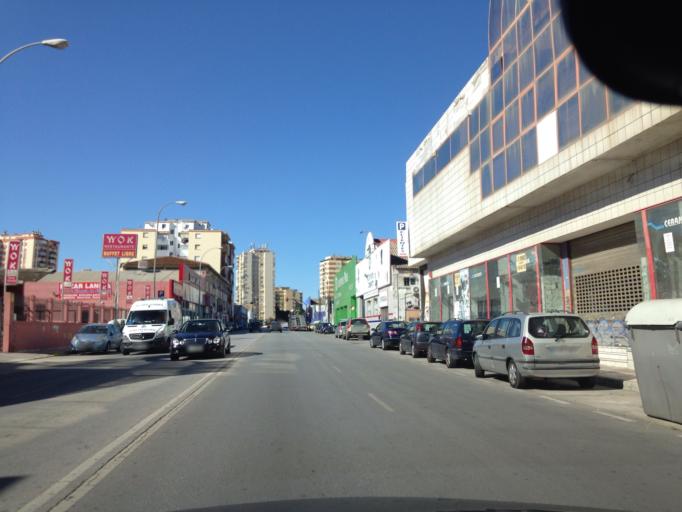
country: ES
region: Andalusia
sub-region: Provincia de Malaga
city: Malaga
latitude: 36.6920
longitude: -4.4504
